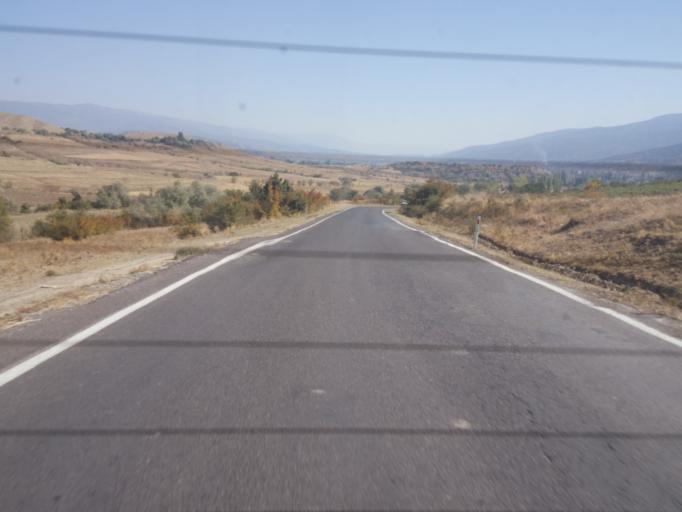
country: TR
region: Kastamonu
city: Tosya
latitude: 40.9856
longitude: 34.0814
